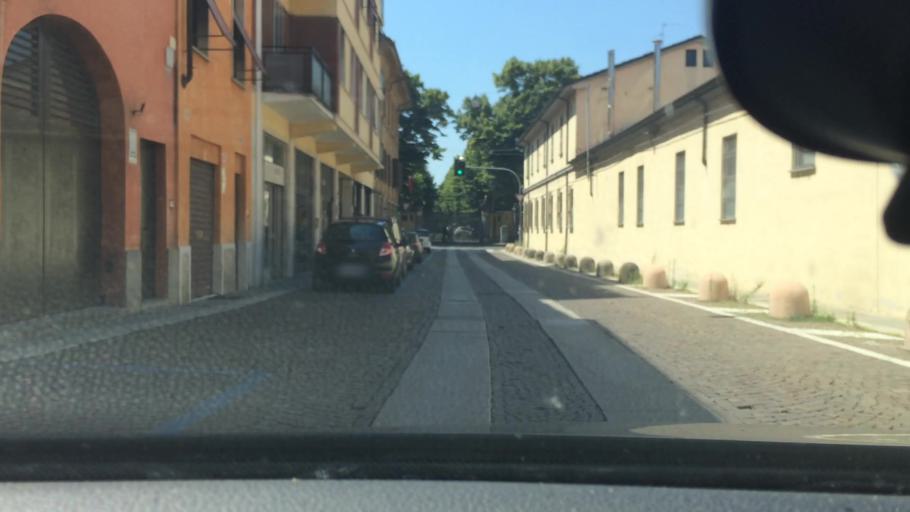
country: IT
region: Emilia-Romagna
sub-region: Provincia di Piacenza
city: Piacenza
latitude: 45.0527
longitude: 9.6847
